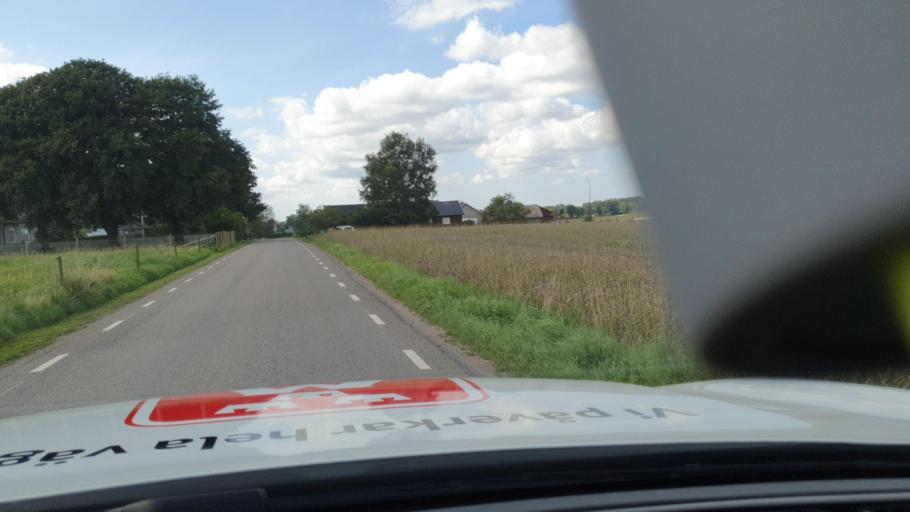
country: SE
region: Halland
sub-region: Laholms Kommun
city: Laholm
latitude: 56.4538
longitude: 13.1740
